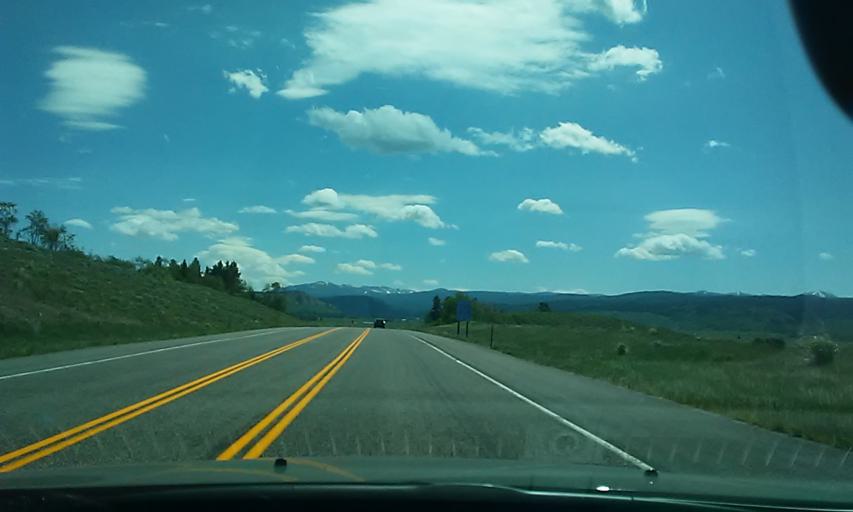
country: US
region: Wyoming
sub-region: Teton County
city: Jackson
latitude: 43.8388
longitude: -110.4470
